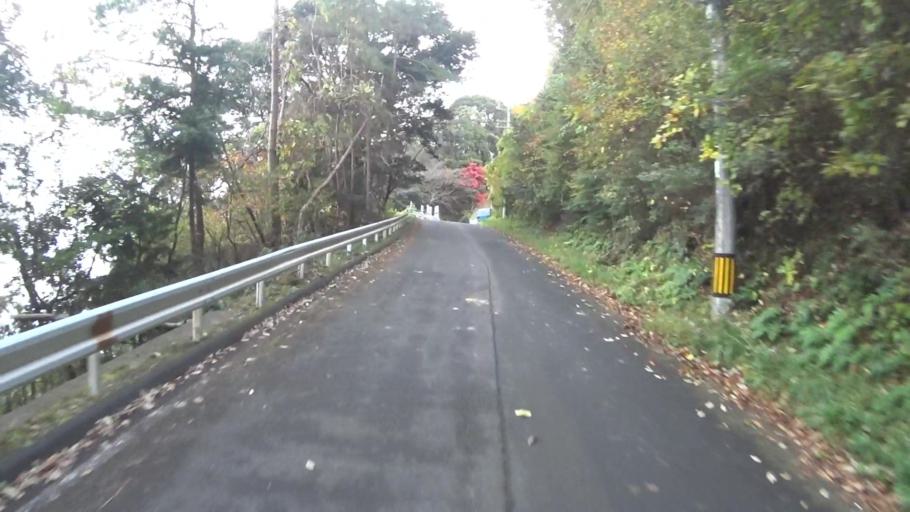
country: JP
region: Kyoto
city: Maizuru
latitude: 35.5780
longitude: 135.4479
